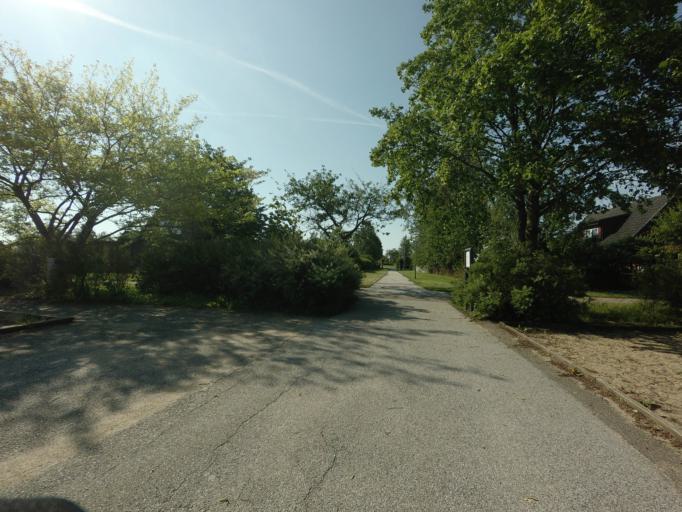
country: SE
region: Skane
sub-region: Malmo
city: Oxie
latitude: 55.4930
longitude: 13.1095
